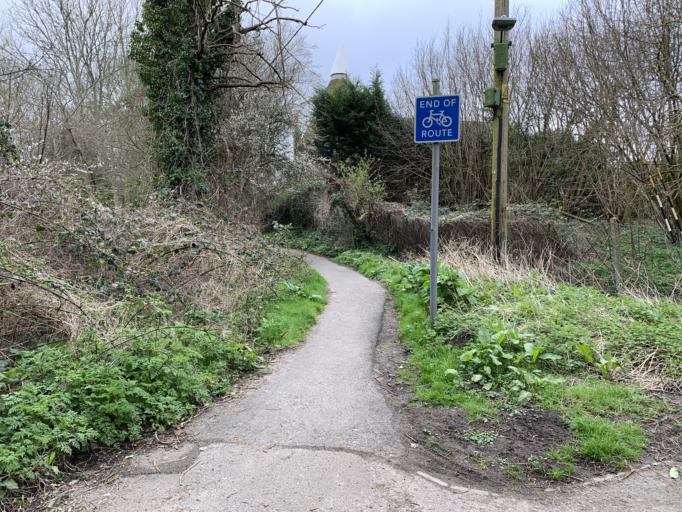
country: GB
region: England
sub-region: East Sussex
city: Uckfield
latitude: 50.9704
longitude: 0.0915
